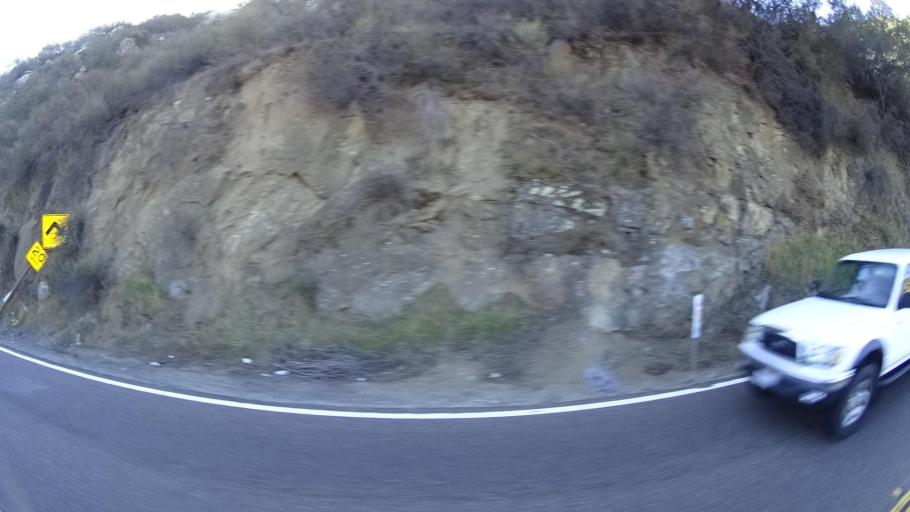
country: US
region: California
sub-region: San Diego County
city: Jamul
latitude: 32.6529
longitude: -116.7902
